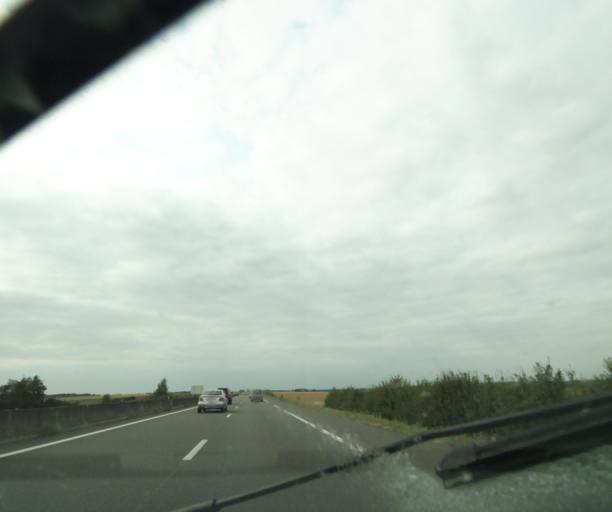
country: FR
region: Centre
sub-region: Departement d'Indre-et-Loire
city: Neuvy-le-Roi
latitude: 47.5681
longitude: 0.5869
